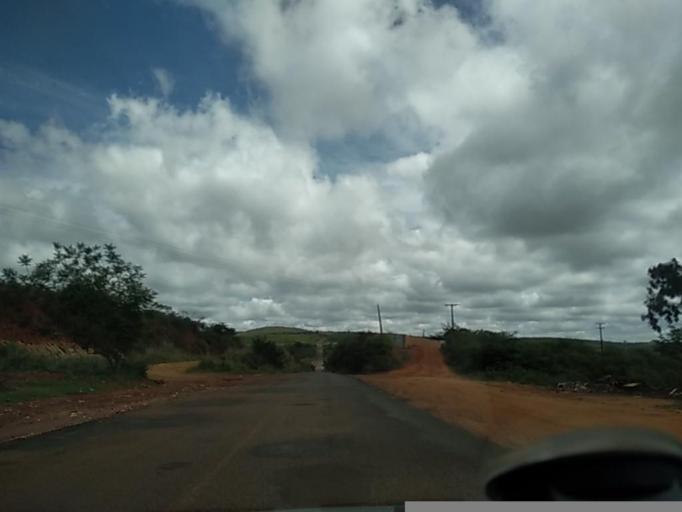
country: BR
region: Bahia
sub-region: Caetite
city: Caetite
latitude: -14.0487
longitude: -42.4851
